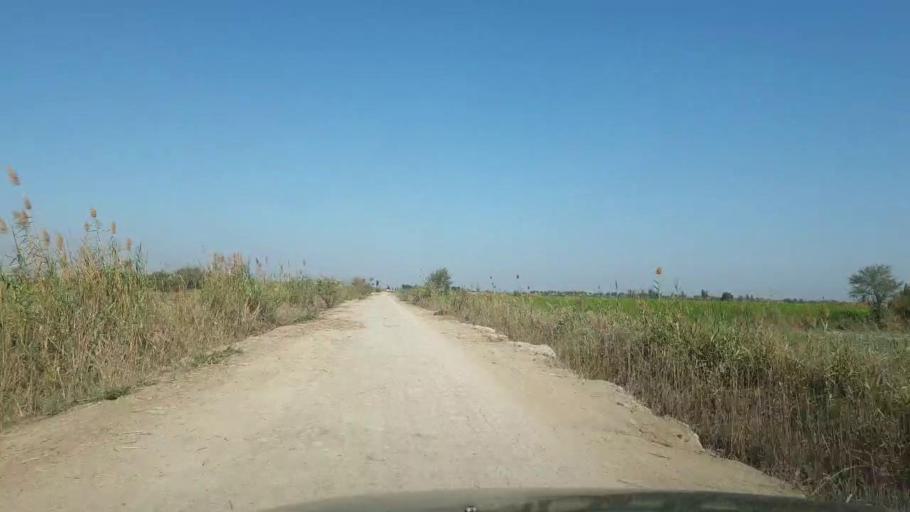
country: PK
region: Sindh
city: Mirpur Khas
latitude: 25.5911
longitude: 69.0557
